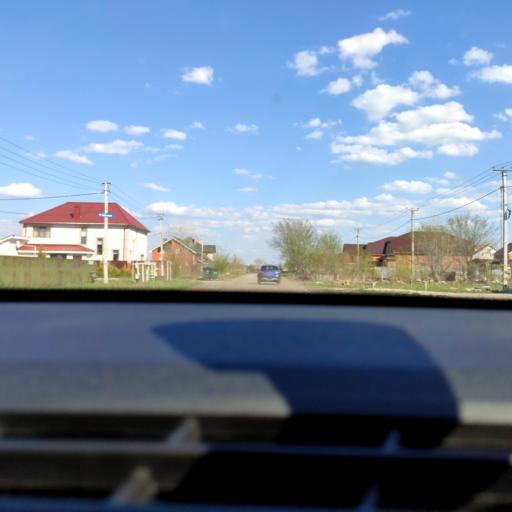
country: RU
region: Samara
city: Tol'yatti
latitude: 53.5555
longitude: 49.3745
